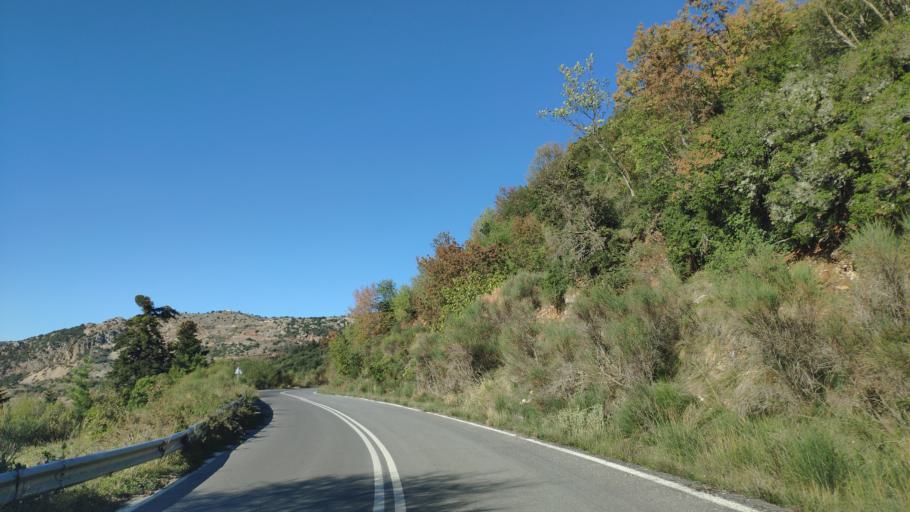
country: GR
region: Peloponnese
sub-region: Nomos Arkadias
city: Dimitsana
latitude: 37.5705
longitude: 22.0613
